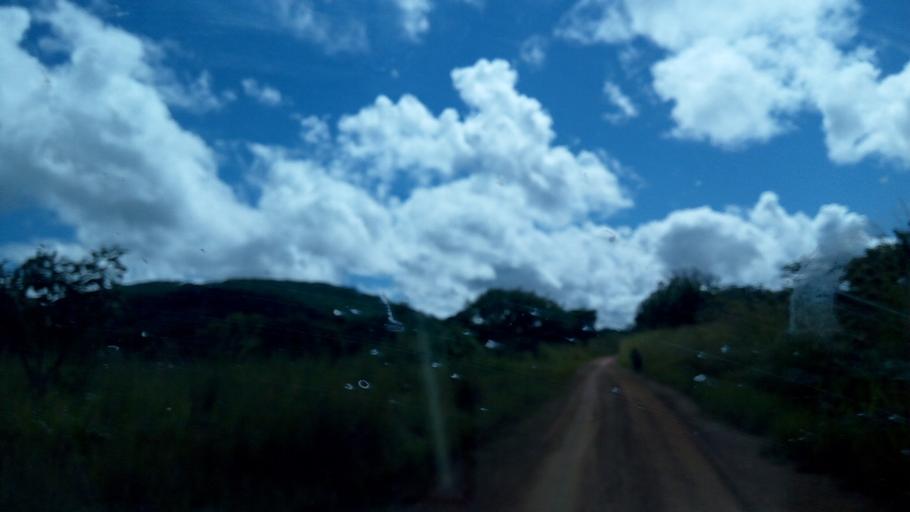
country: ZM
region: Northern
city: Kaputa
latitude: -8.2225
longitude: 29.0523
